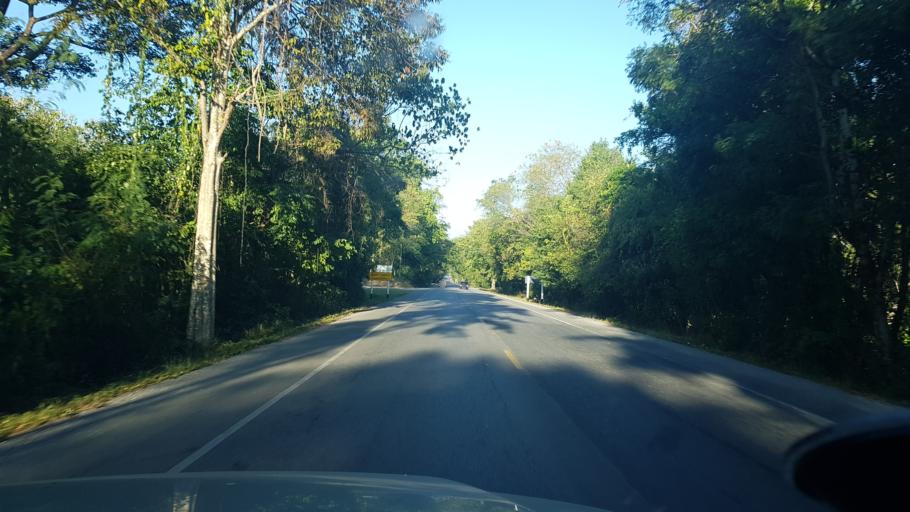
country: TH
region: Khon Kaen
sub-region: Amphoe Phu Pha Man
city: Phu Pha Man
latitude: 16.6262
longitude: 101.8508
